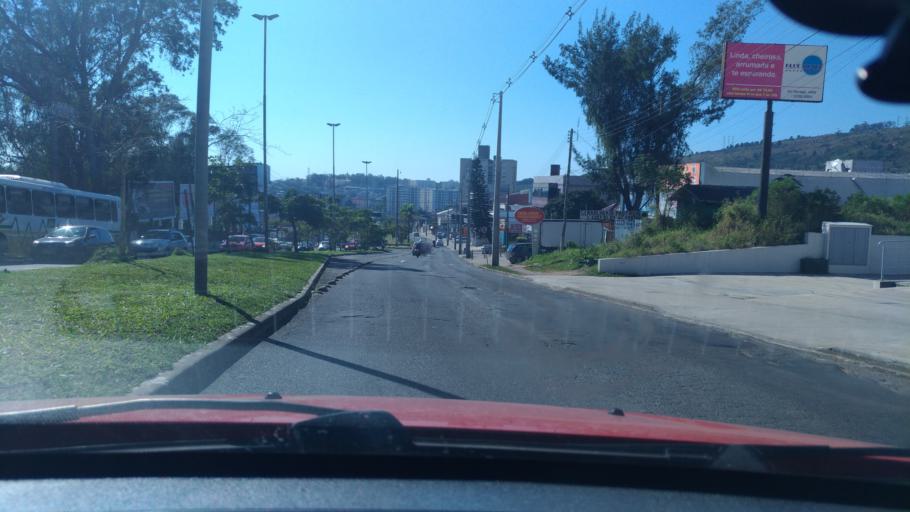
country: BR
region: Rio Grande do Sul
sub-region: Porto Alegre
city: Porto Alegre
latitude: -30.0429
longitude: -51.1371
